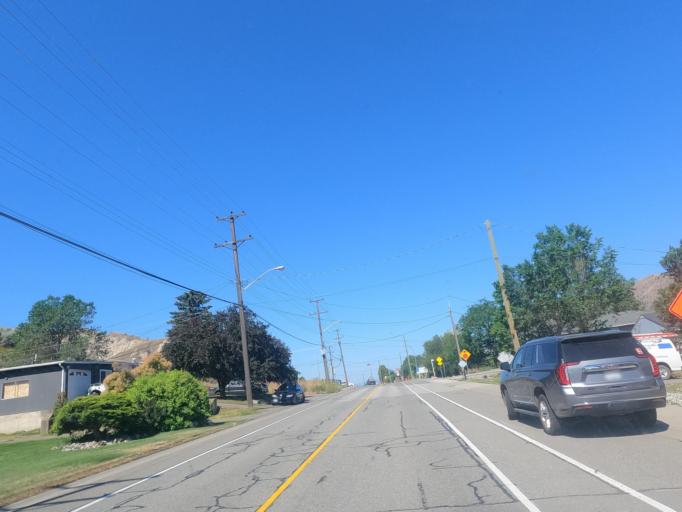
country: CA
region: British Columbia
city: Kamloops
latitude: 50.6761
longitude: -120.2604
